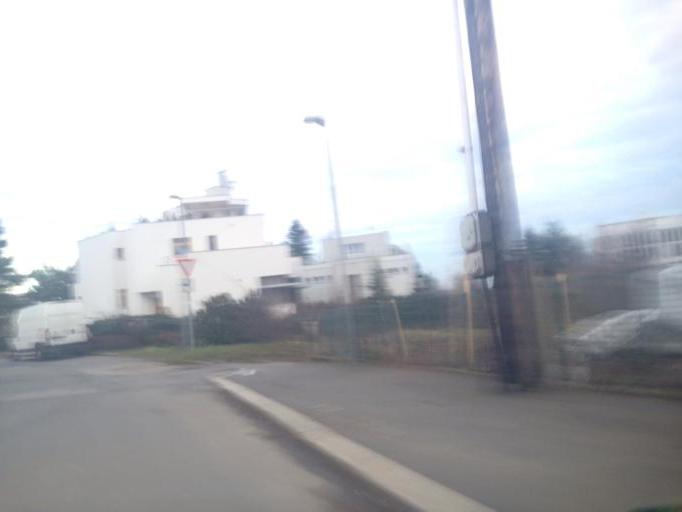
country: CZ
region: Praha
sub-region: Praha 1
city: Mala Strana
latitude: 50.1157
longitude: 14.3869
